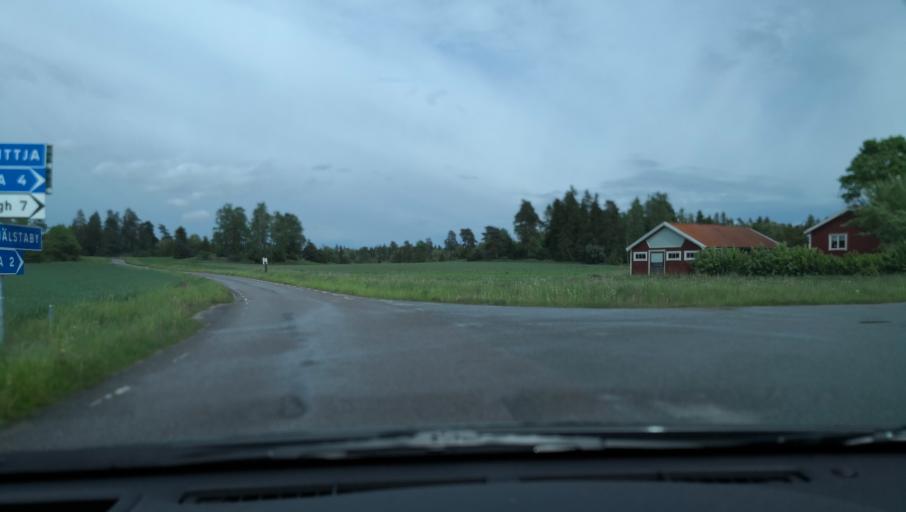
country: SE
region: Uppsala
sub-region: Enkopings Kommun
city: Orsundsbro
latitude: 59.7042
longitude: 17.4188
